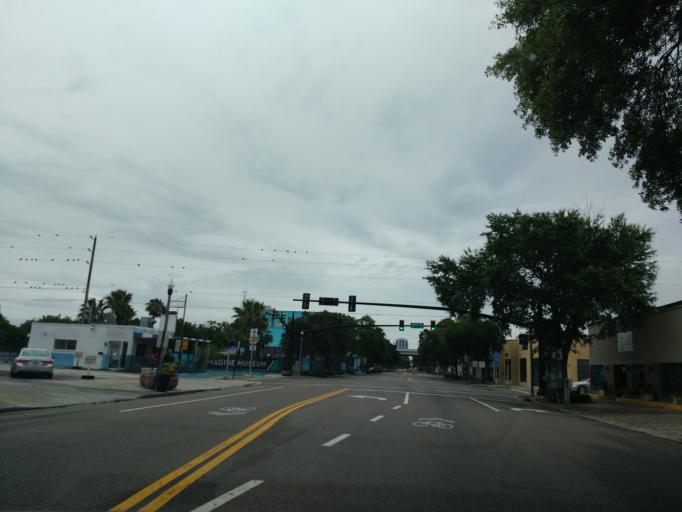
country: US
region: Florida
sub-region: Pinellas County
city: Saint Petersburg
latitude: 27.7711
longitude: -82.6608
